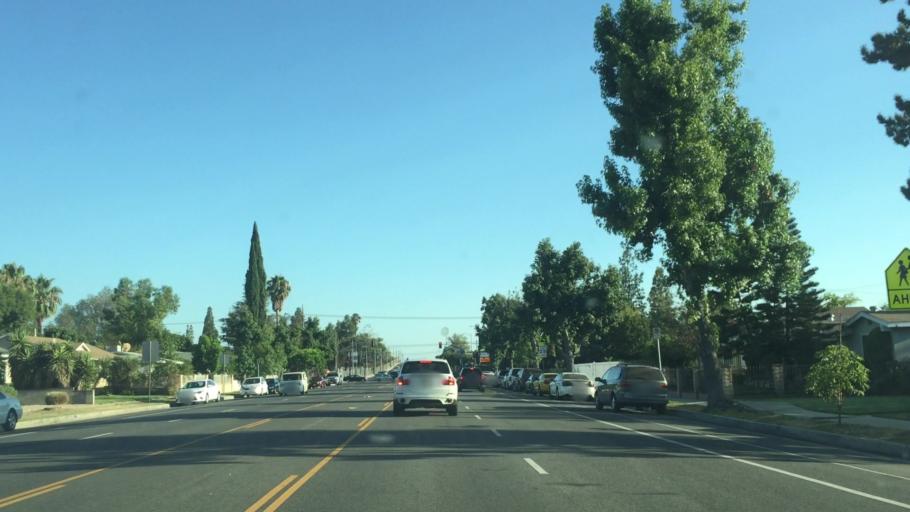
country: US
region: California
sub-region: Los Angeles County
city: San Fernando
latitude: 34.2517
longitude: -118.4850
